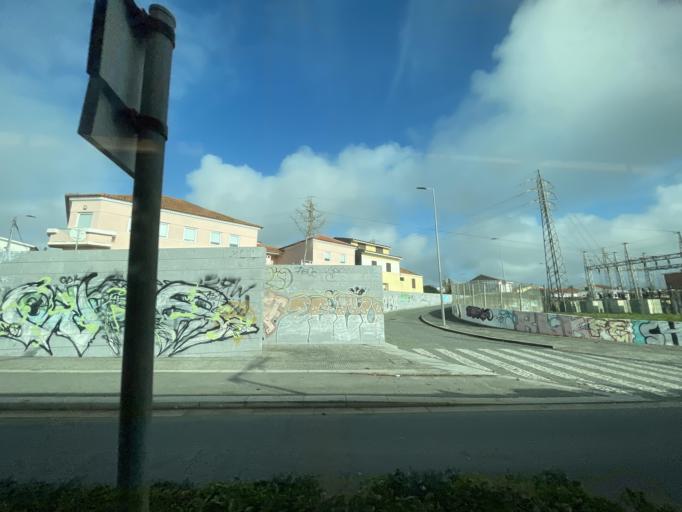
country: PT
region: Porto
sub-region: Vila do Conde
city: Vila do Conde
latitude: 41.3556
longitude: -8.7369
